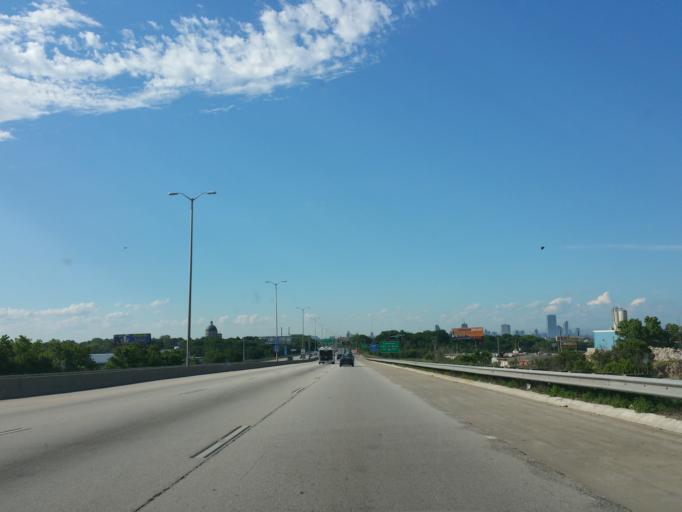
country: US
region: Wisconsin
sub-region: Milwaukee County
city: Saint Francis
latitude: 42.9892
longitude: -87.9142
